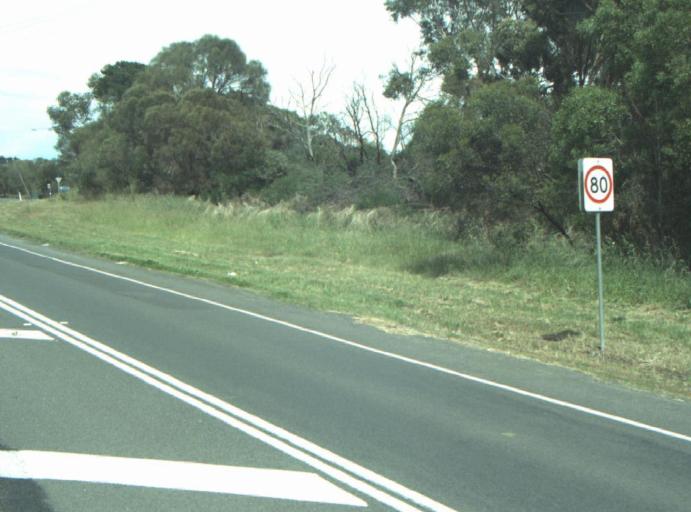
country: AU
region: Victoria
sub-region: Greater Geelong
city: Clifton Springs
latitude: -38.1591
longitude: 144.5847
